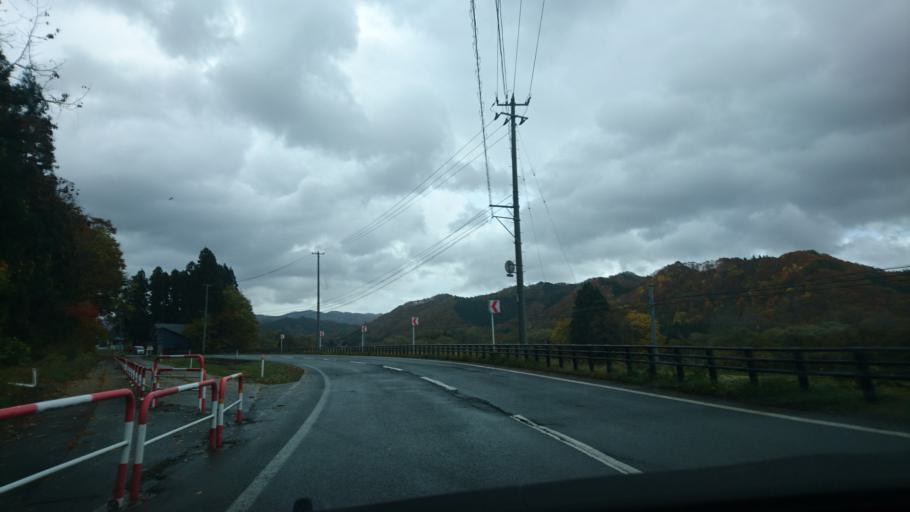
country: JP
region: Akita
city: Kakunodatemachi
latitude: 39.4761
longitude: 140.7895
